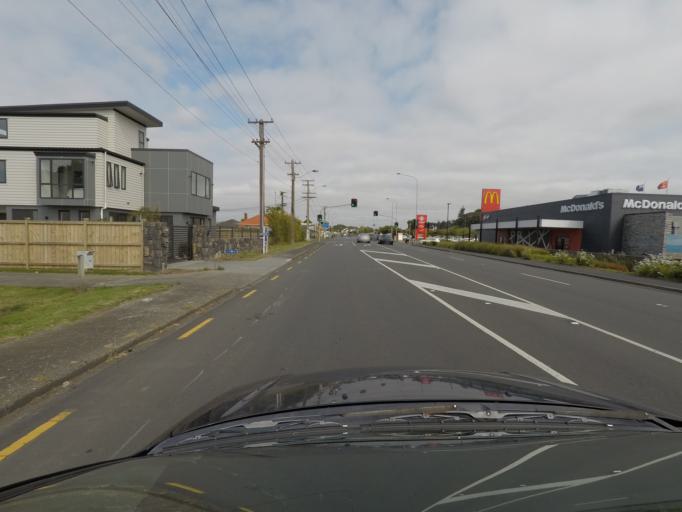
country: NZ
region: Auckland
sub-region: Auckland
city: Auckland
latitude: -36.9072
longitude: 174.7339
